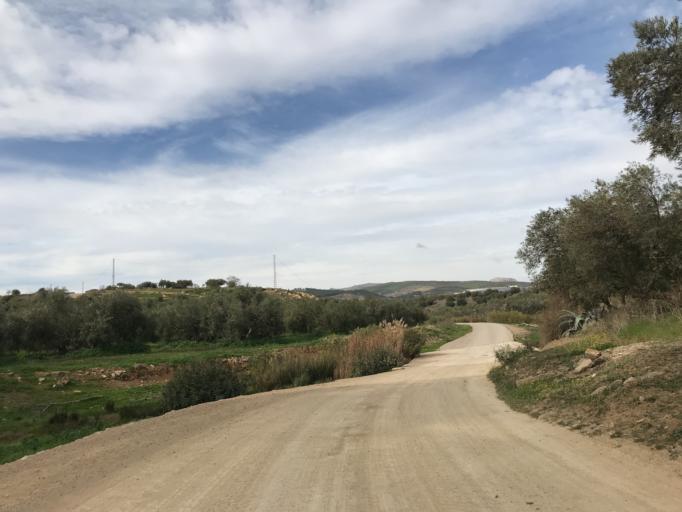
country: ES
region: Andalusia
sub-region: Provincia de Malaga
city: Ardales
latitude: 36.8829
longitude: -4.8563
